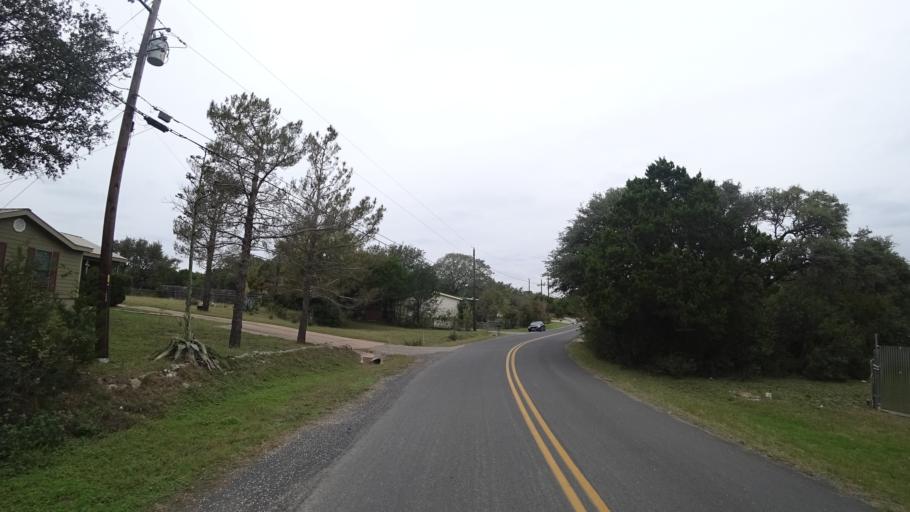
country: US
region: Texas
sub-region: Travis County
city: Lakeway
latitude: 30.3705
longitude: -97.9379
